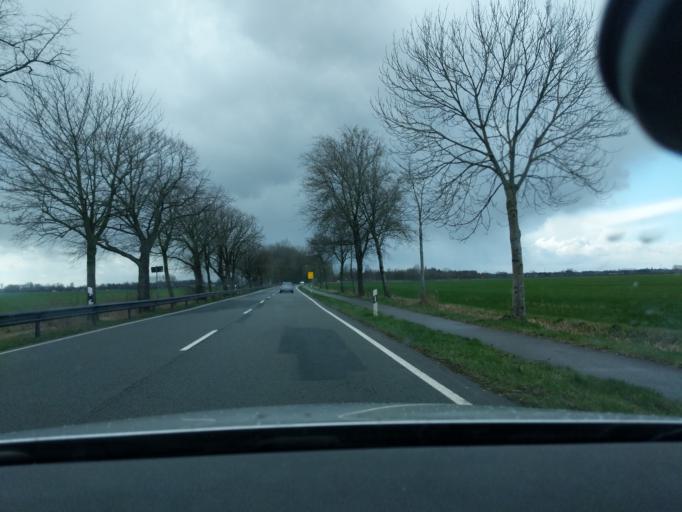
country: DE
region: Lower Saxony
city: Osten
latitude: 53.7042
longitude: 9.2072
